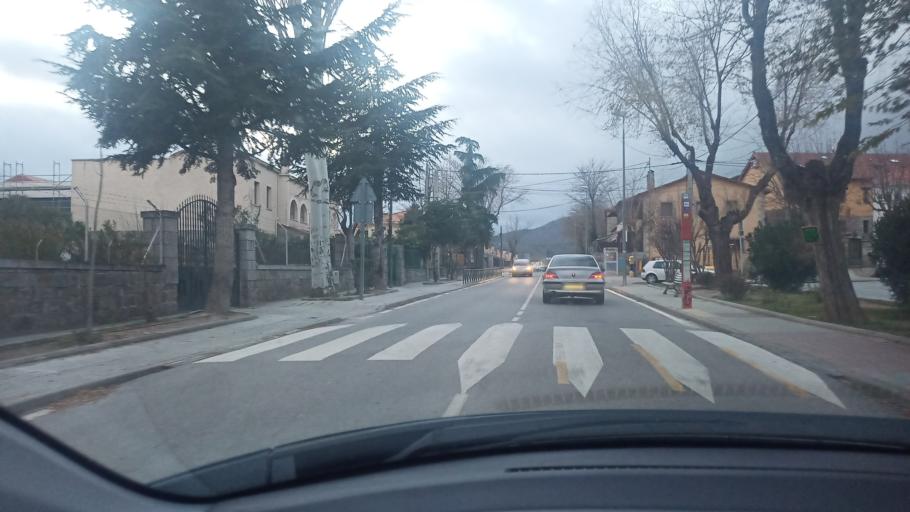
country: ES
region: Madrid
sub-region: Provincia de Madrid
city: Zarzalejo
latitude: 40.5397
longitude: -4.1636
